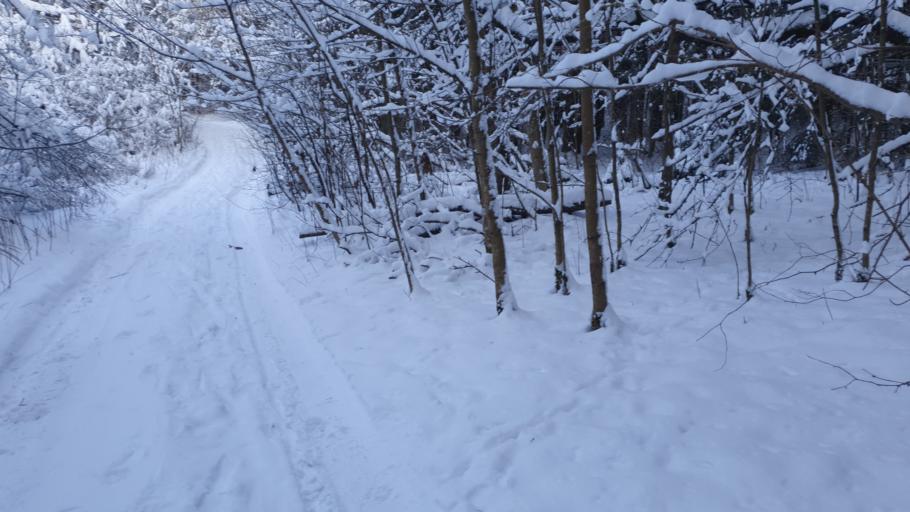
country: LT
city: Skaidiskes
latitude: 54.6417
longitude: 25.4164
